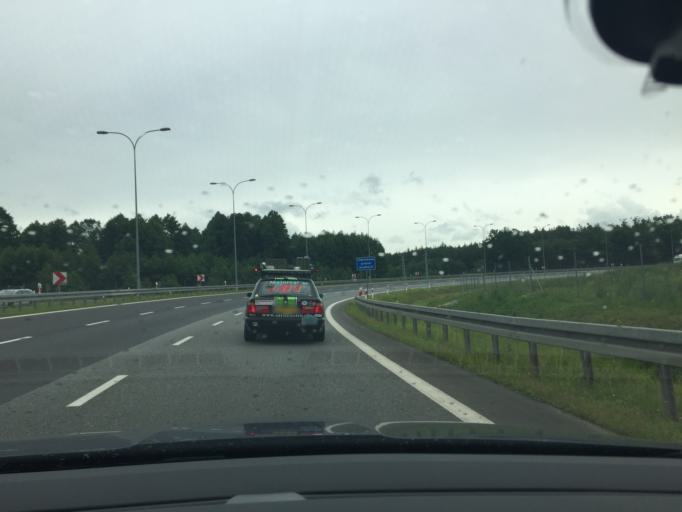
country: PL
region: Kujawsko-Pomorskie
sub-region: Powiat swiecki
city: Warlubie
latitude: 53.4699
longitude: 18.6134
